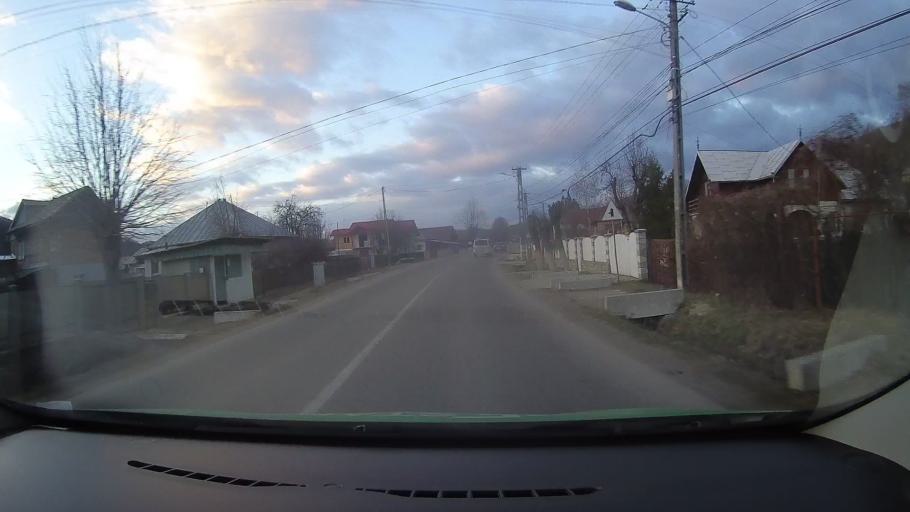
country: RO
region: Dambovita
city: Iedera de Jos
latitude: 45.0222
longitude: 25.6364
